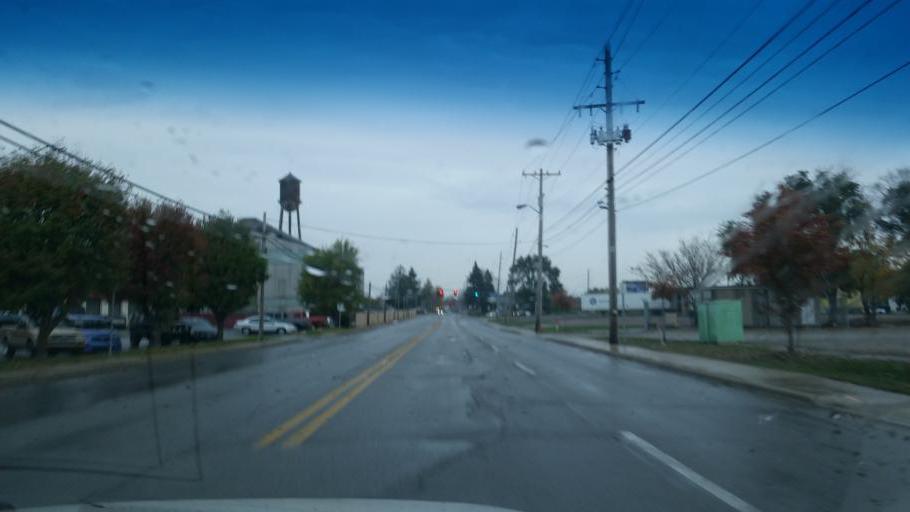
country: US
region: Indiana
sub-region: Howard County
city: Kokomo
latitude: 40.4717
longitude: -86.1268
